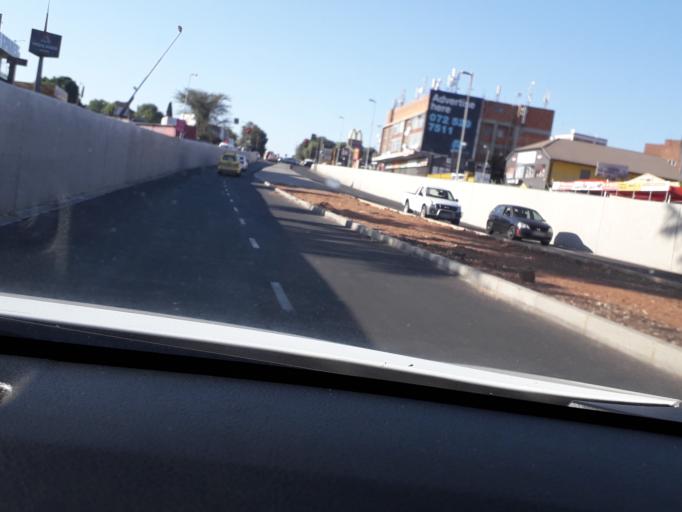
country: ZA
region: Gauteng
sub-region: City of Johannesburg Metropolitan Municipality
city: Johannesburg
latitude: -26.1380
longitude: 28.0866
